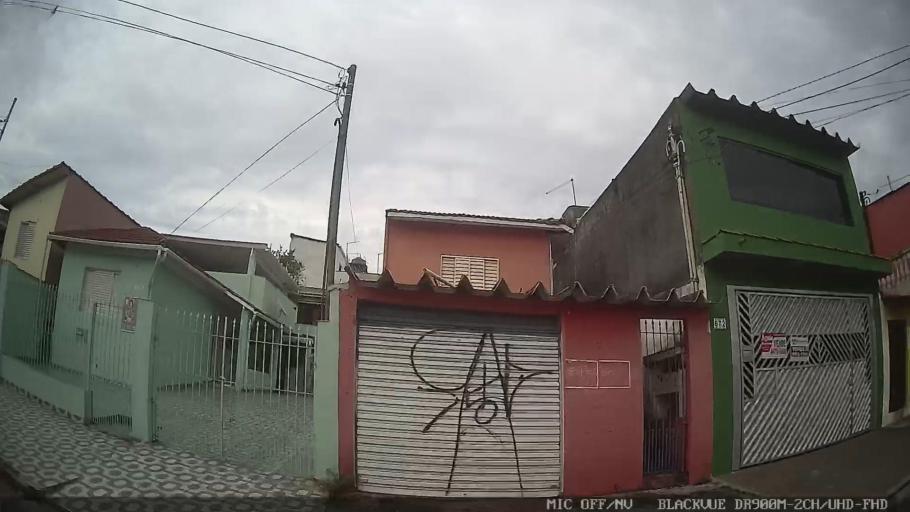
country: BR
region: Sao Paulo
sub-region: Maua
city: Maua
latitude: -23.6320
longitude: -46.4764
